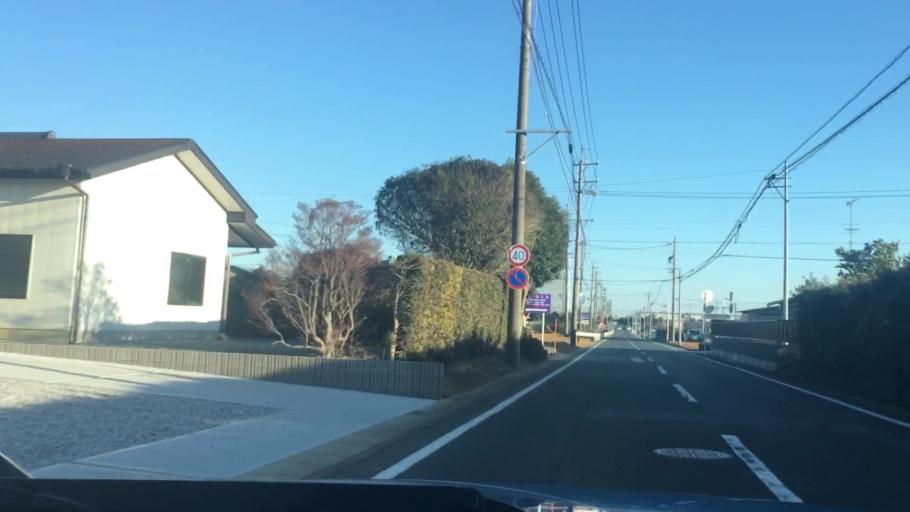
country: JP
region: Shizuoka
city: Hamamatsu
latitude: 34.7639
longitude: 137.6867
